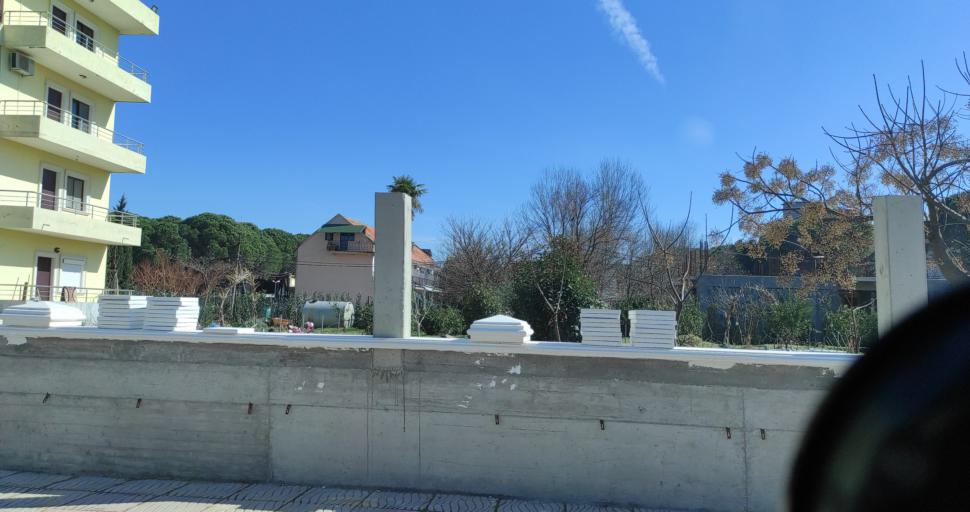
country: AL
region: Shkoder
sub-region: Rrethi i Shkodres
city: Velipoje
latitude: 41.8645
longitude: 19.4121
